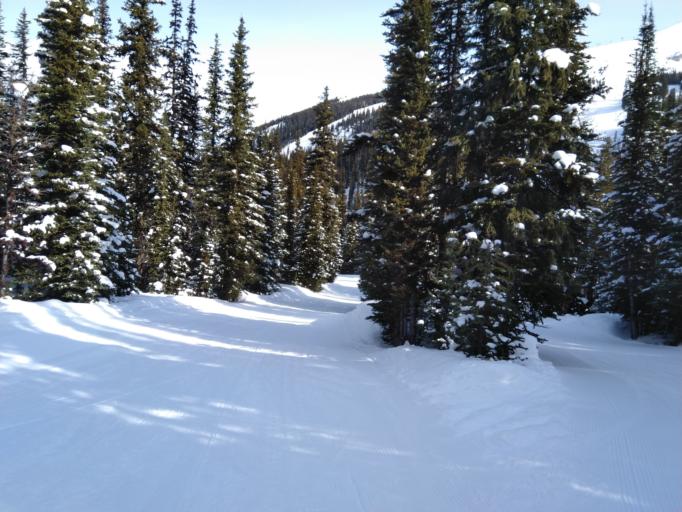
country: CA
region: Alberta
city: Banff
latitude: 51.0865
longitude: -115.7679
